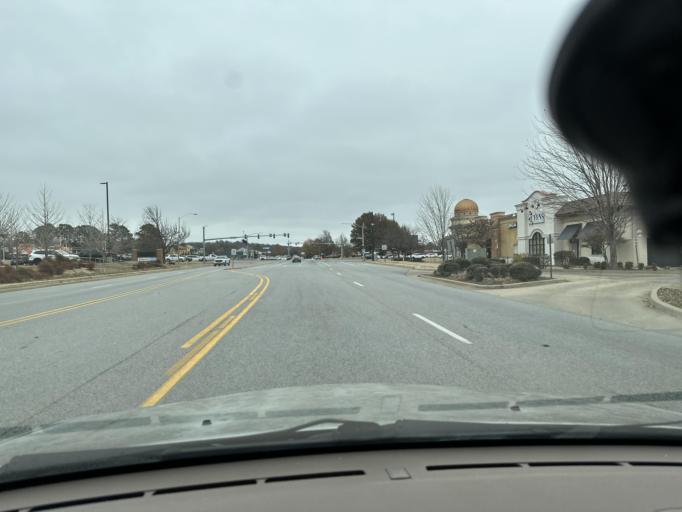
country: US
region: Arkansas
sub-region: Washington County
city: Johnson
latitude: 36.1235
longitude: -94.1464
